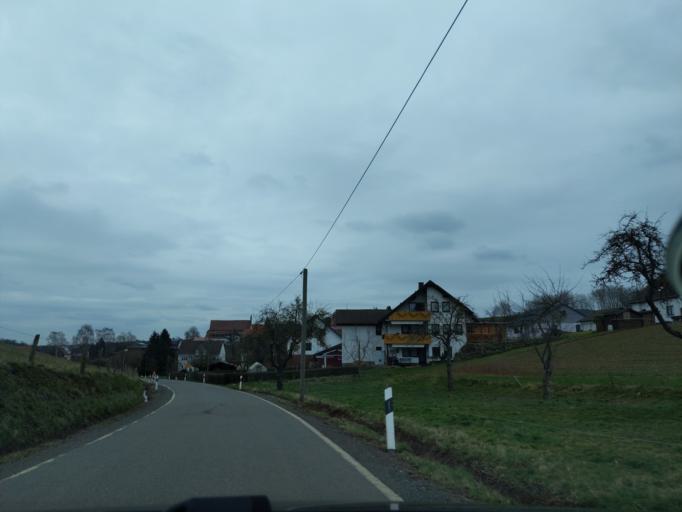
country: DE
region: Hesse
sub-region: Regierungsbezirk Kassel
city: Bad Arolsen
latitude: 51.3242
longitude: 9.0466
